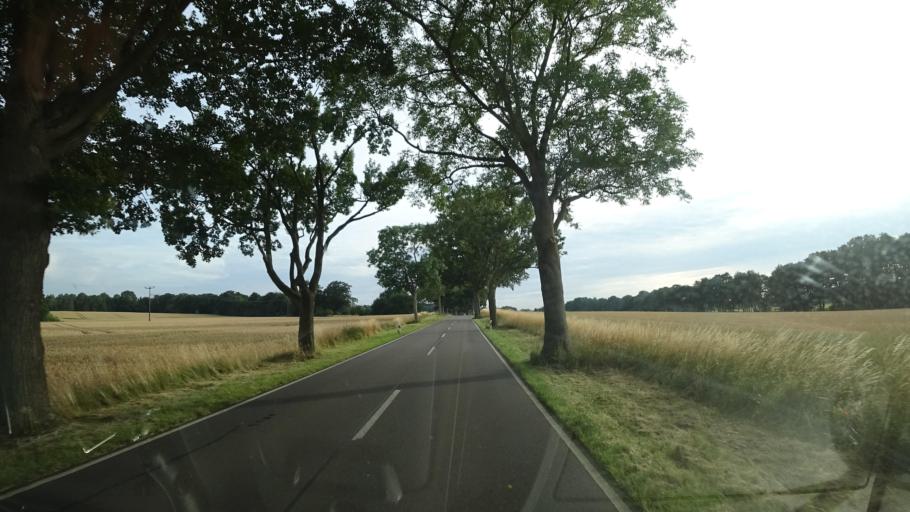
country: DE
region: Mecklenburg-Vorpommern
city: Ostseebad Binz
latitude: 54.4163
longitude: 13.5389
